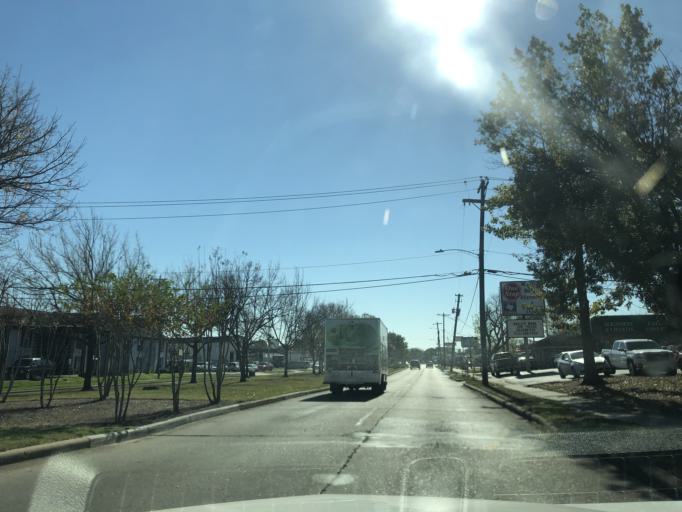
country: US
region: Texas
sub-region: Harris County
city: Bellaire
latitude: 29.6972
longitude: -95.4931
